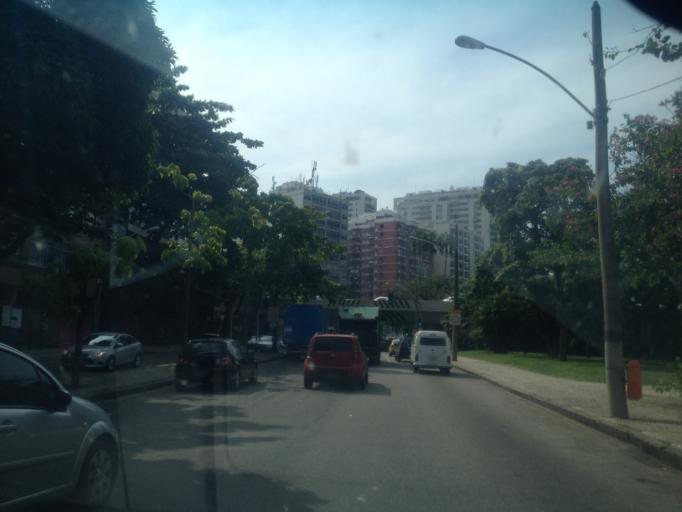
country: BR
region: Rio de Janeiro
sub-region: Rio De Janeiro
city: Rio de Janeiro
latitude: -22.9615
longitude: -43.2047
